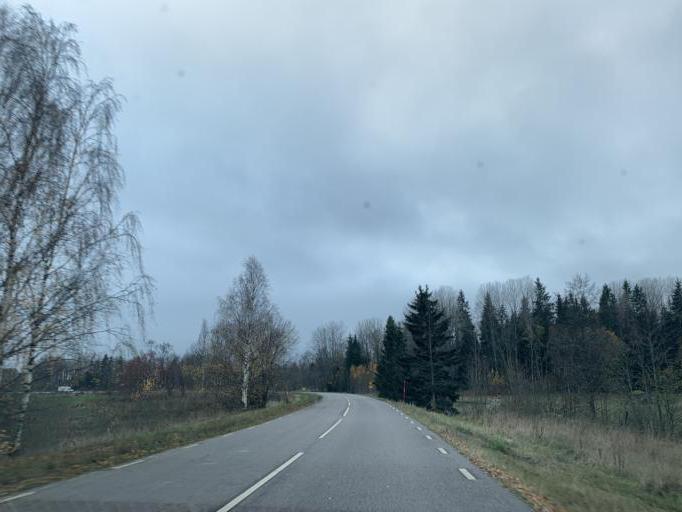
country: SE
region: Vaestmanland
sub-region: Surahammars Kommun
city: Ramnas
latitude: 59.7636
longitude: 16.1862
